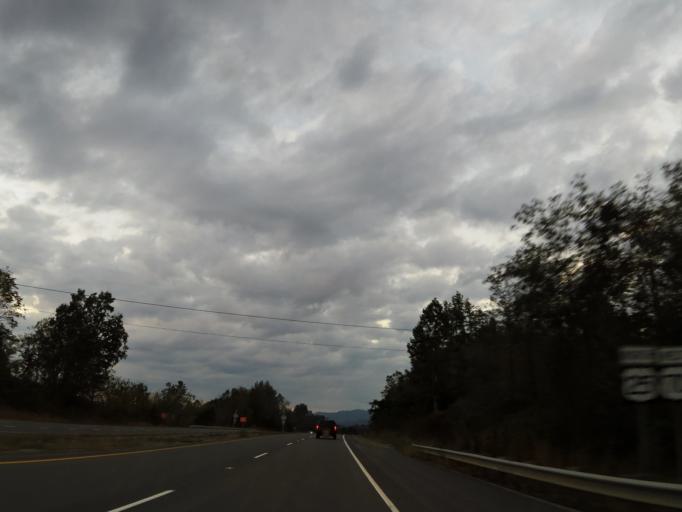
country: US
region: North Carolina
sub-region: Buncombe County
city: Weaverville
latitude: 35.7499
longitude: -82.6191
